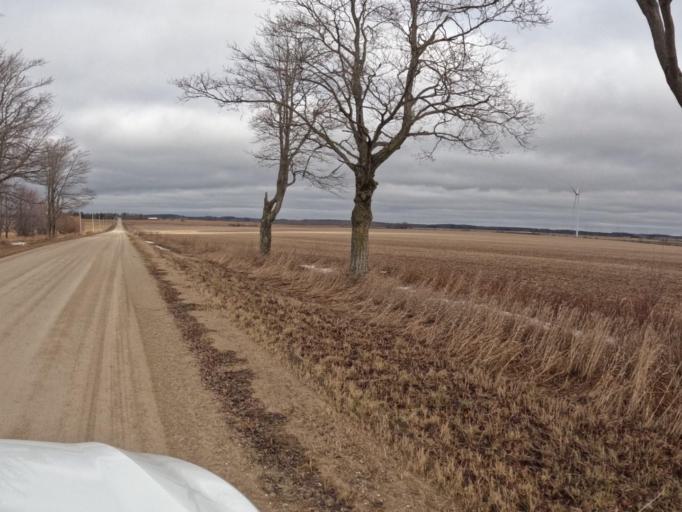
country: CA
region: Ontario
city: Shelburne
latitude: 43.9978
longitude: -80.4089
